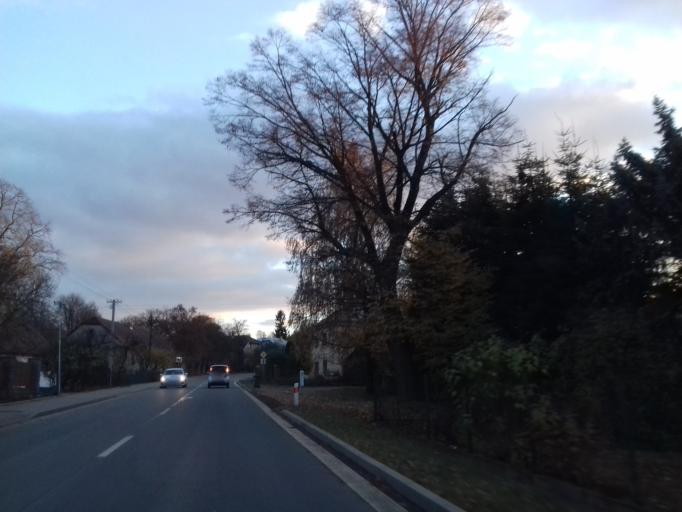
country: CZ
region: Pardubicky
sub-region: Okres Chrudim
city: Hlinsko
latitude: 49.7902
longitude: 15.9256
